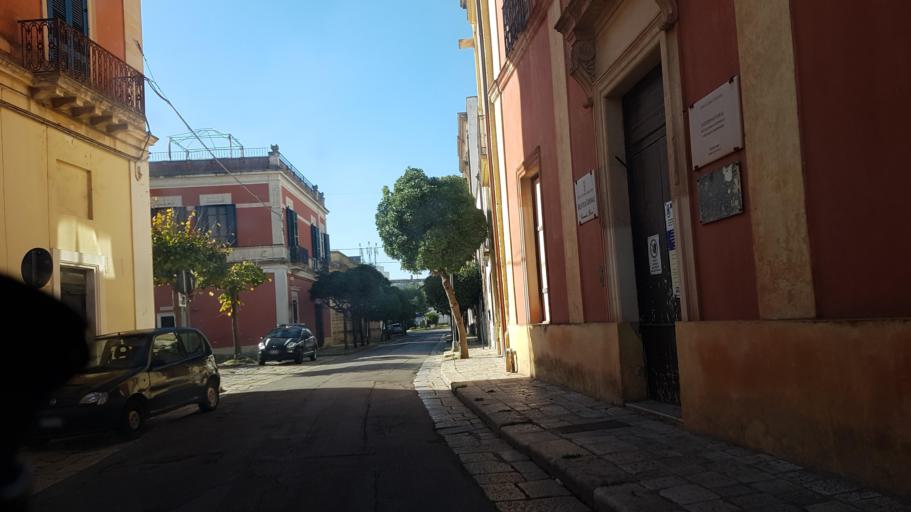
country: IT
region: Apulia
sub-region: Provincia di Lecce
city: Campi Salentina
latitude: 40.3984
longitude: 18.0188
